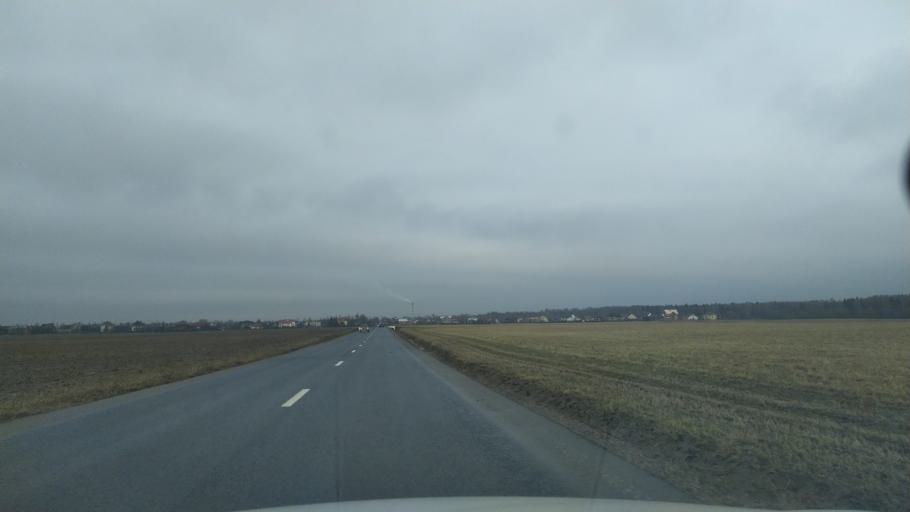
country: RU
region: St.-Petersburg
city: Aleksandrovskaya
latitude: 59.7166
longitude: 30.3377
